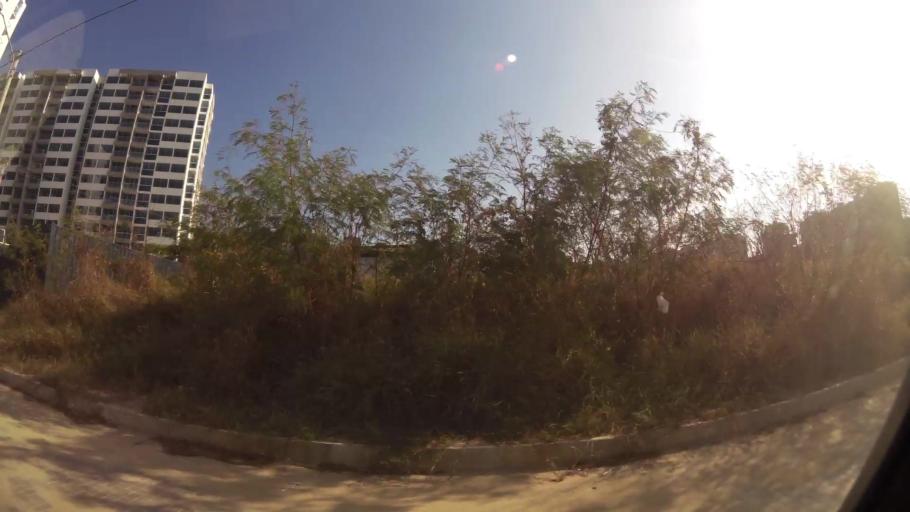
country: CO
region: Atlantico
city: Barranquilla
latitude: 11.0064
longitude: -74.8373
